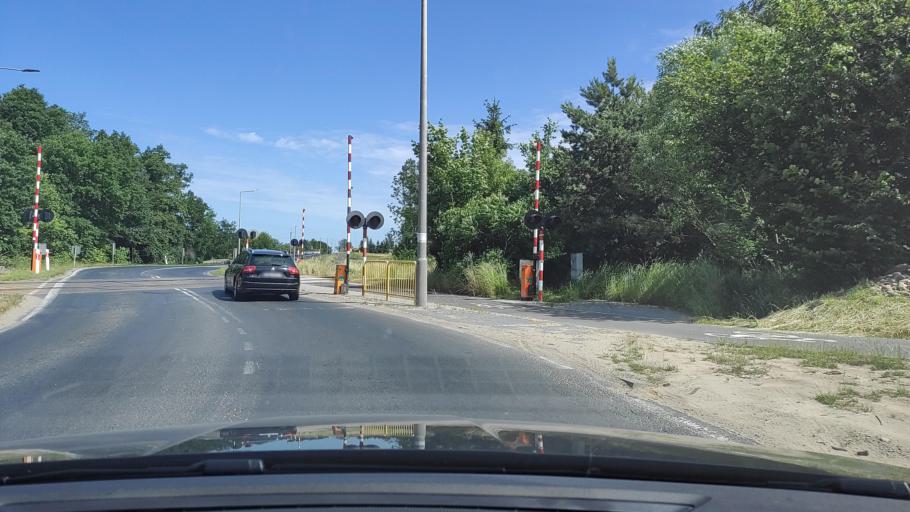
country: PL
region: Greater Poland Voivodeship
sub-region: Powiat poznanski
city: Czerwonak
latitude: 52.4919
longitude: 16.9775
